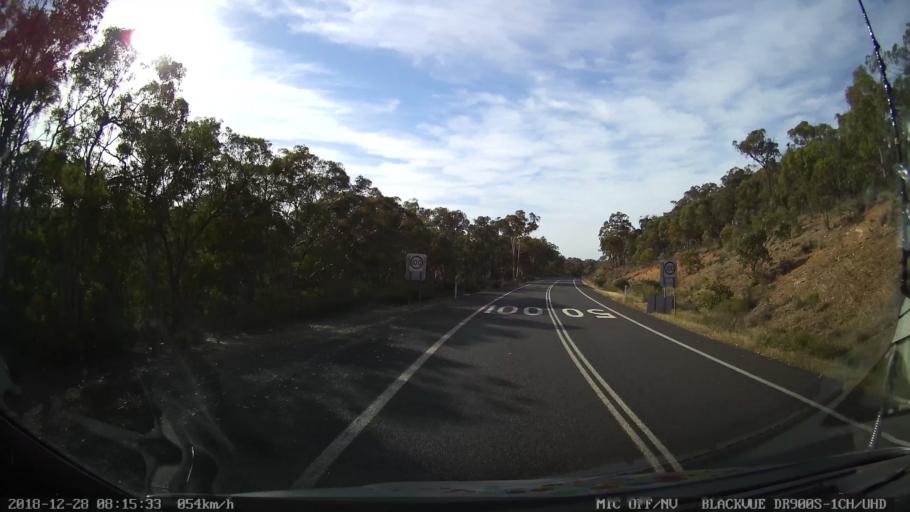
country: AU
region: New South Wales
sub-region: Blayney
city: Blayney
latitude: -33.8239
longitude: 149.3289
